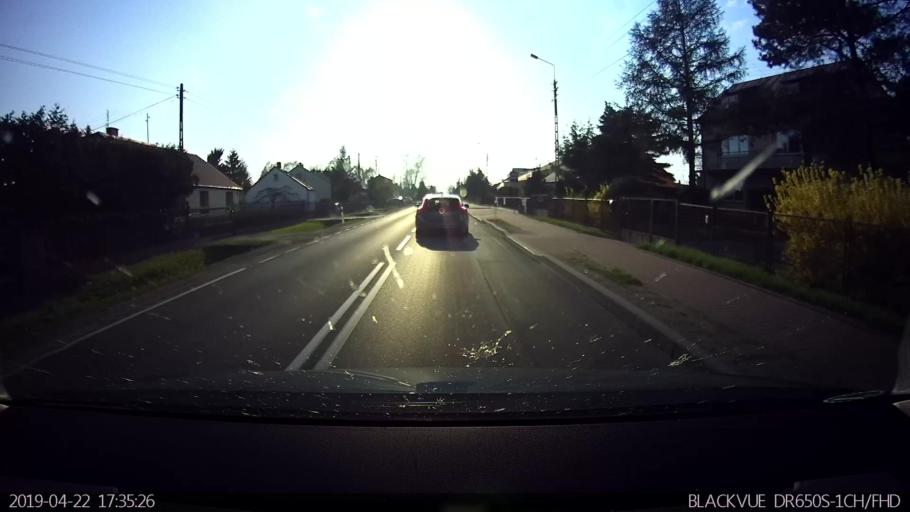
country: PL
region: Masovian Voivodeship
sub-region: Powiat sokolowski
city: Sokolow Podlaski
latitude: 52.4074
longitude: 22.2030
